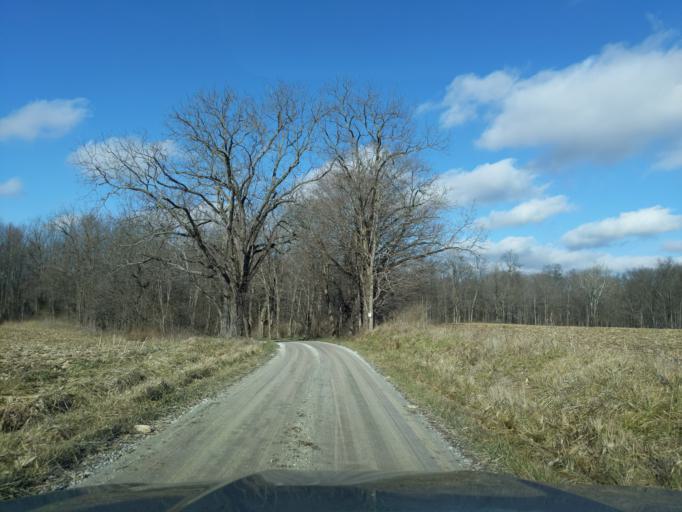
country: US
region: Indiana
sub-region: Decatur County
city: Greensburg
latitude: 39.2465
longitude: -85.4842
